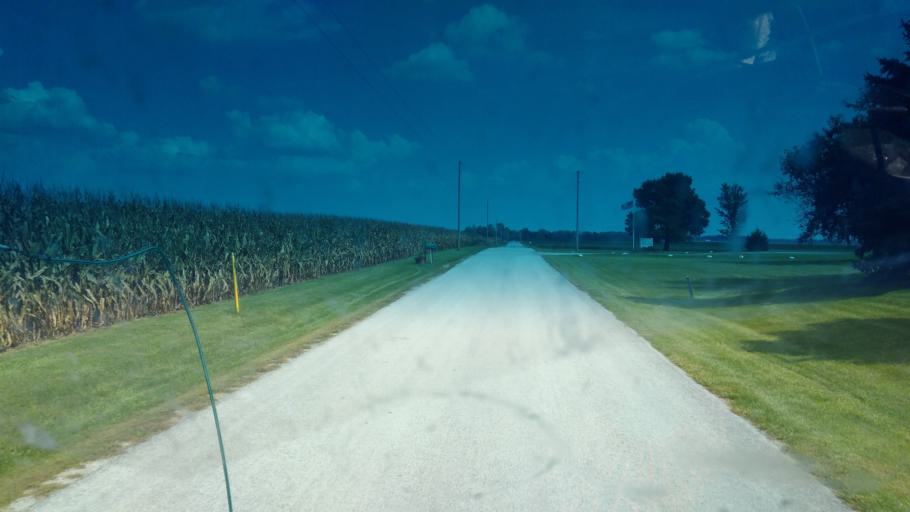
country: US
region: Ohio
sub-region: Hardin County
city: Kenton
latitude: 40.6611
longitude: -83.6915
